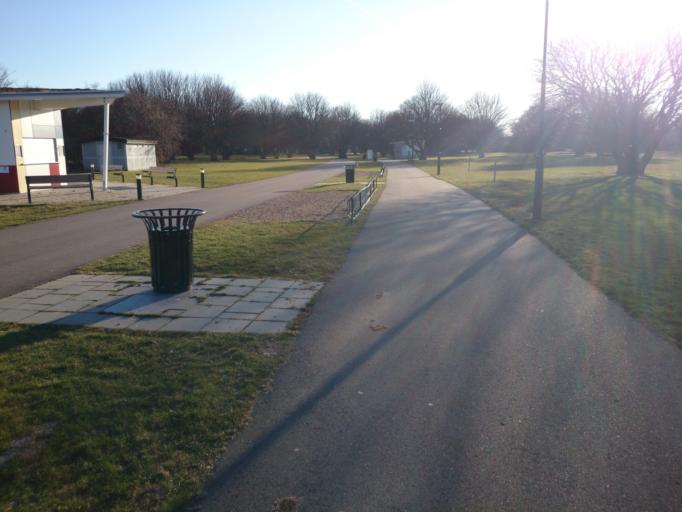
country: SE
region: Skane
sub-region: Malmo
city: Bunkeflostrand
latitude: 55.5738
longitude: 12.9057
